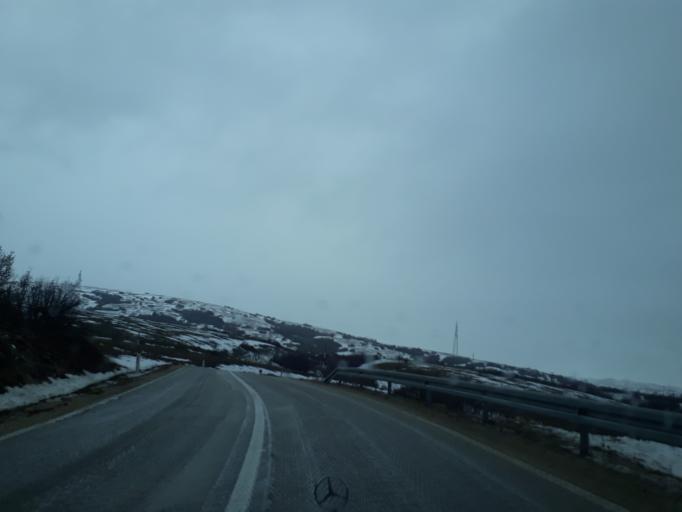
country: BA
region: Federation of Bosnia and Herzegovina
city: Tomislavgrad
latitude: 43.8008
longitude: 17.2068
